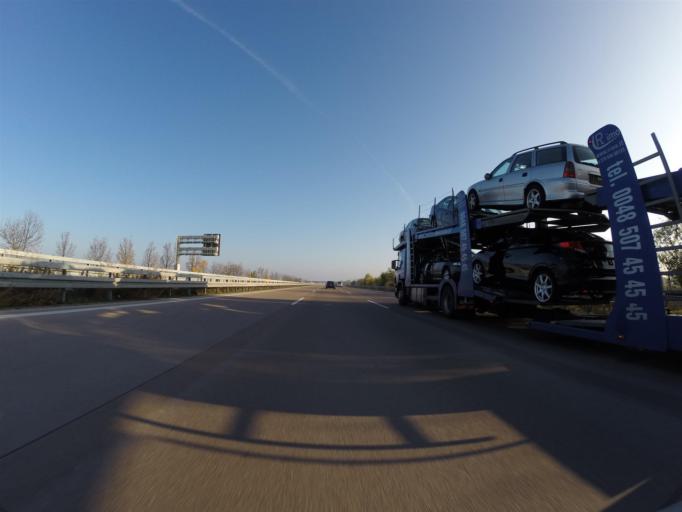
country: DE
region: Saxony-Anhalt
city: Tollwitz
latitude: 51.2569
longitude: 12.0831
